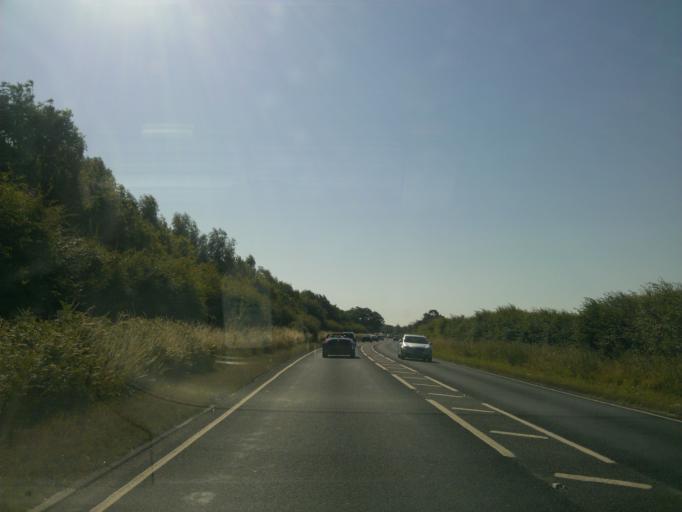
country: GB
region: England
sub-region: Essex
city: Great Bentley
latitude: 51.8656
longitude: 1.0792
